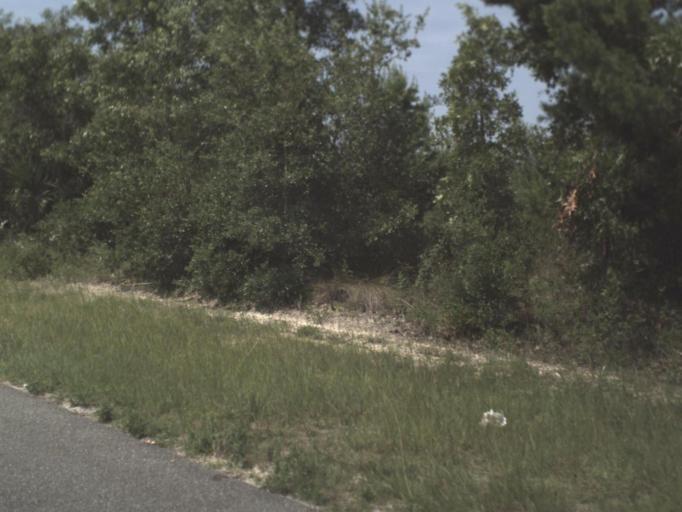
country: US
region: Florida
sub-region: Taylor County
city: Steinhatchee
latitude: 29.6987
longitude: -83.3572
